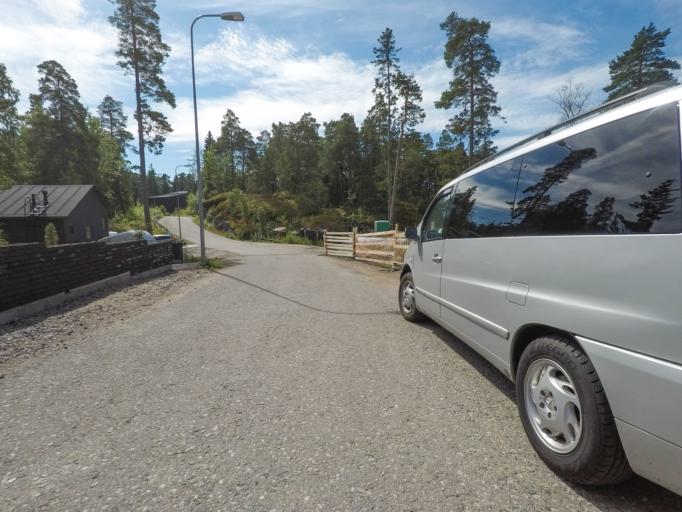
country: FI
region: Uusimaa
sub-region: Helsinki
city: Vantaa
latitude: 60.1675
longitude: 25.0909
